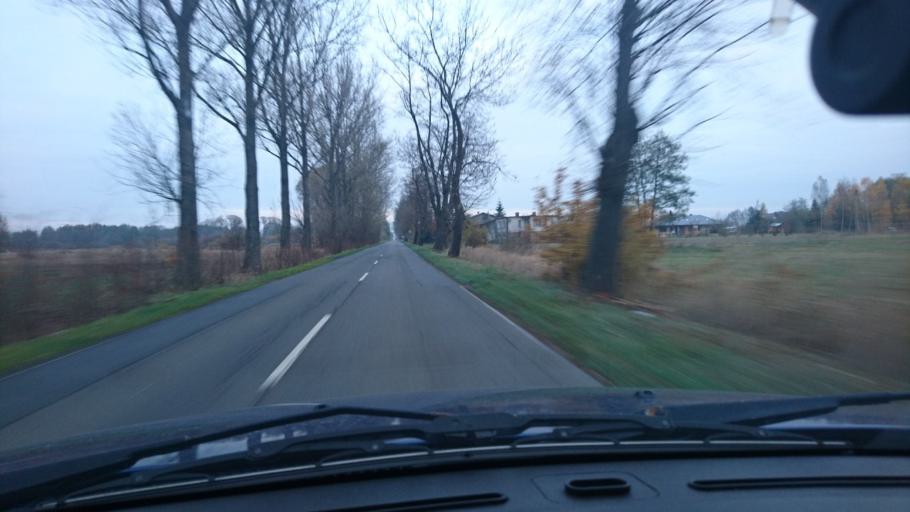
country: PL
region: Greater Poland Voivodeship
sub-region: Powiat ostrowski
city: Odolanow
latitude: 51.5470
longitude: 17.6569
